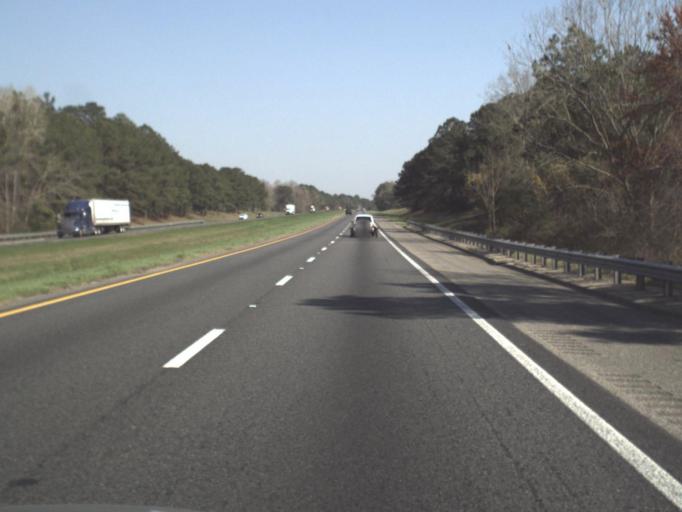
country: US
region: Florida
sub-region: Gadsden County
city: Gretna
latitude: 30.5663
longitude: -84.6596
